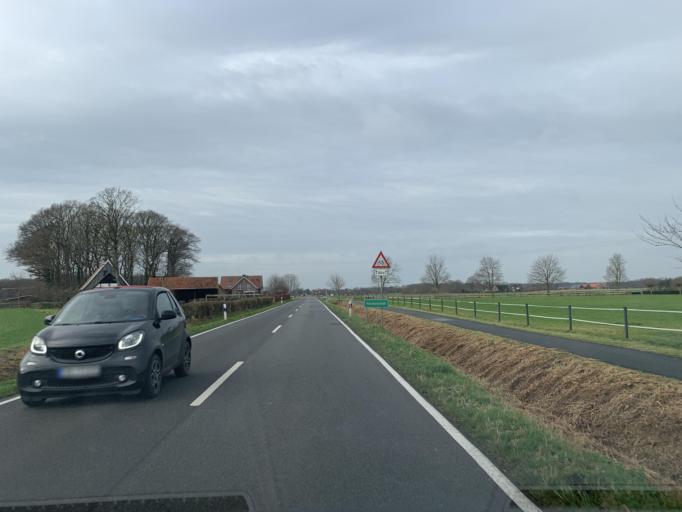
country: DE
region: North Rhine-Westphalia
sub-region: Regierungsbezirk Munster
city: Ascheberg
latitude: 51.8256
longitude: 7.5707
